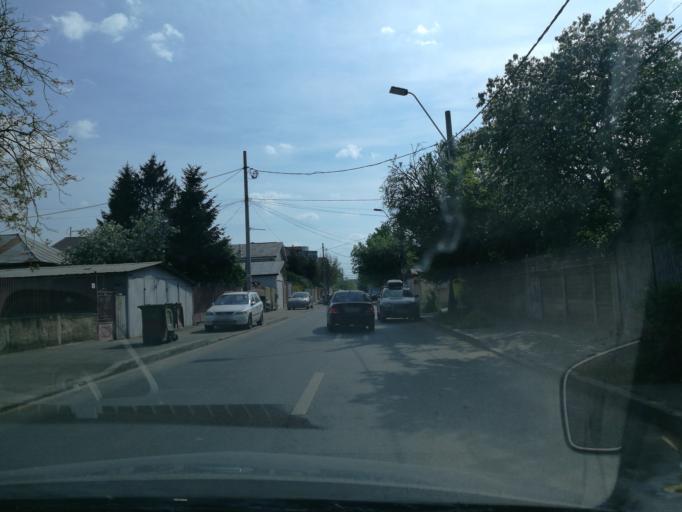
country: RO
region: Ilfov
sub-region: Comuna Chiajna
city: Rosu
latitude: 44.4428
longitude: 26.0274
